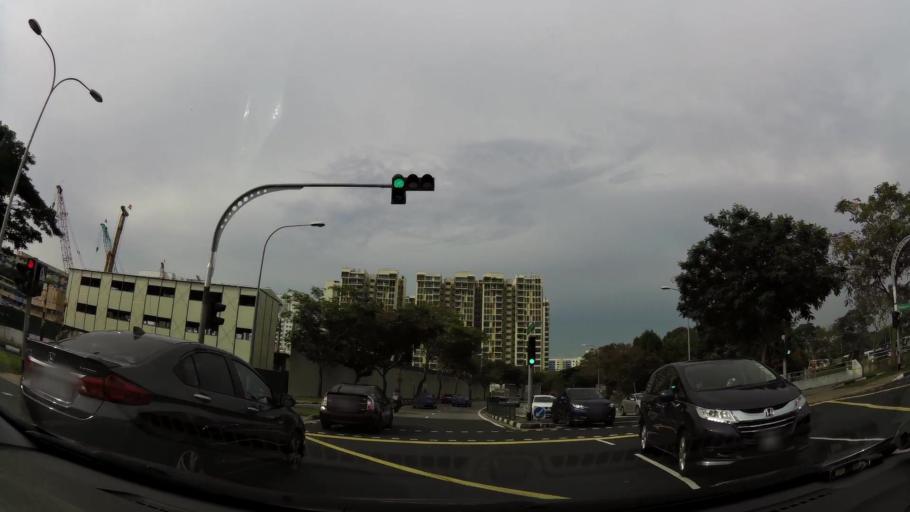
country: SG
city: Singapore
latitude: 1.3618
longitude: 103.8953
